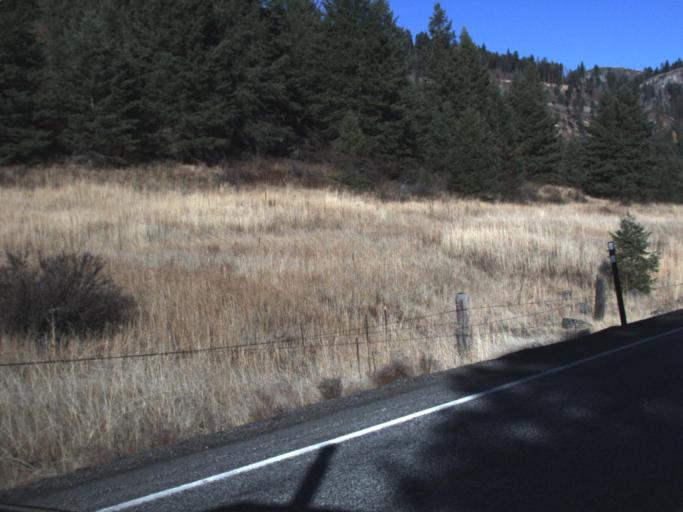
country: US
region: Washington
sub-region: Ferry County
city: Republic
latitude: 48.5620
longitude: -118.7434
